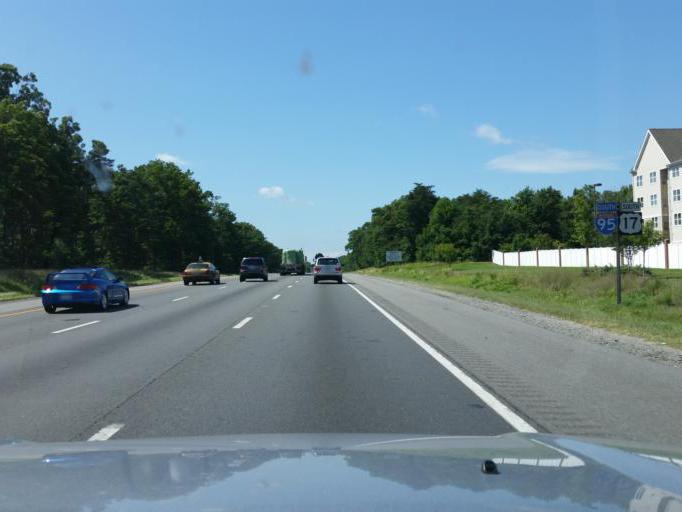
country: US
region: Virginia
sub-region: City of Fredericksburg
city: Fredericksburg
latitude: 38.2877
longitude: -77.5090
